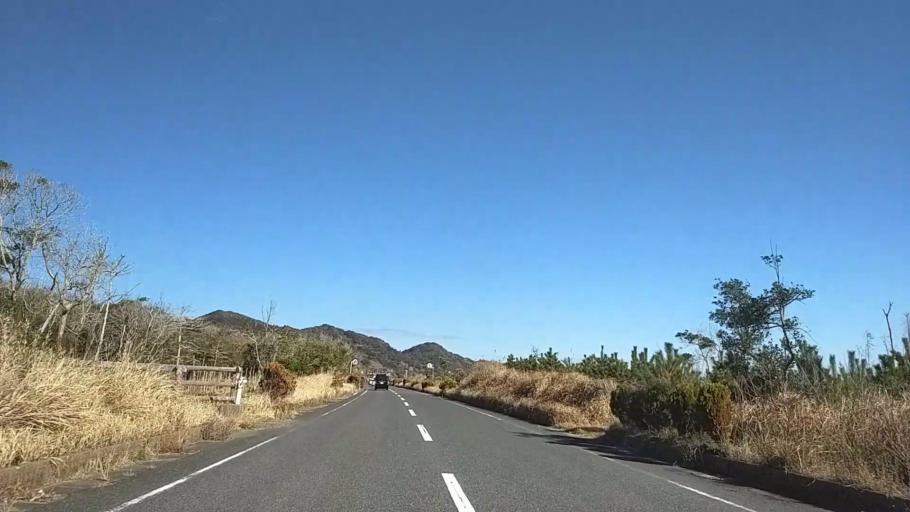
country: JP
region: Chiba
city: Tateyama
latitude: 35.0200
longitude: 139.9883
